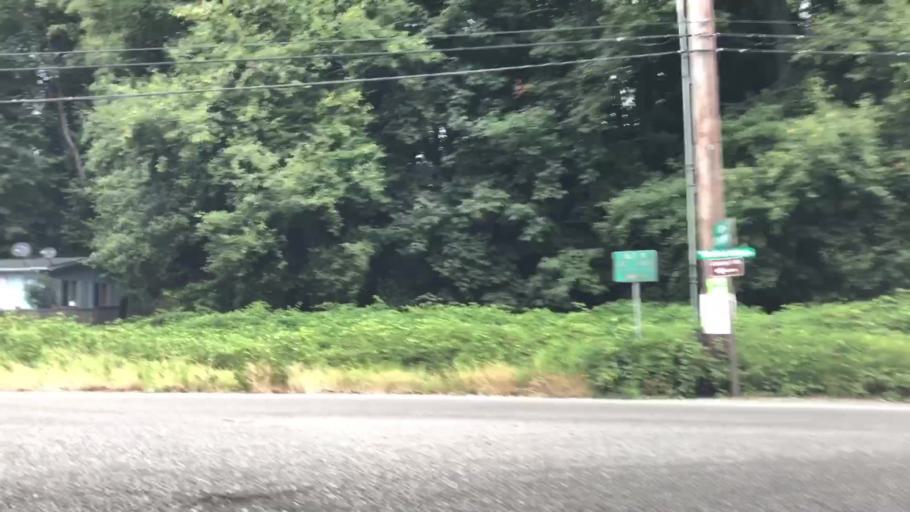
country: US
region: Washington
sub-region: Kitsap County
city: Navy Yard City
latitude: 47.5290
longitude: -122.7037
